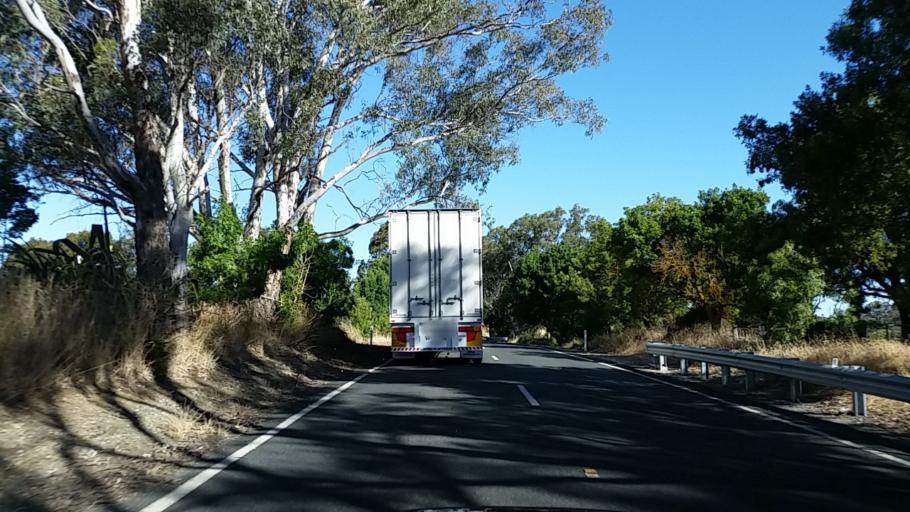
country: AU
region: South Australia
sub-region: Adelaide Hills
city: Birdwood
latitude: -34.7659
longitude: 139.0183
